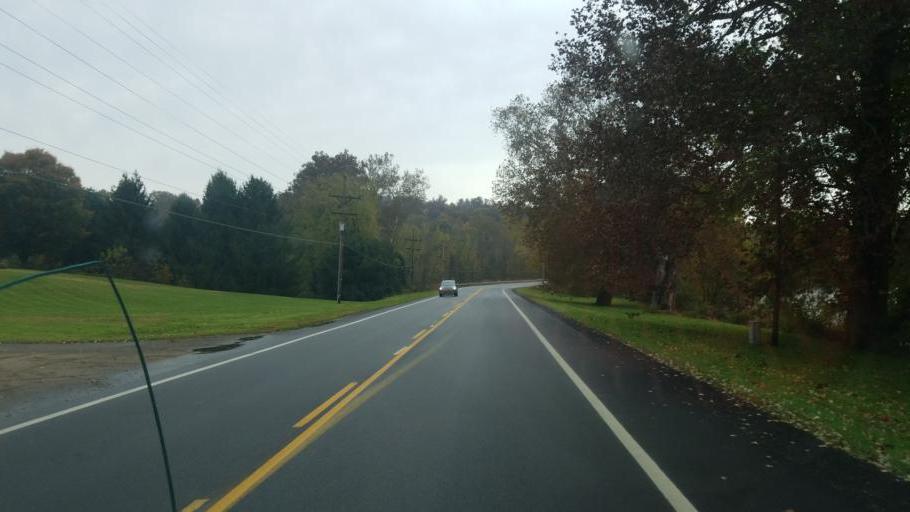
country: US
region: Ohio
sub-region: Washington County
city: Beverly
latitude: 39.5547
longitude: -81.6192
